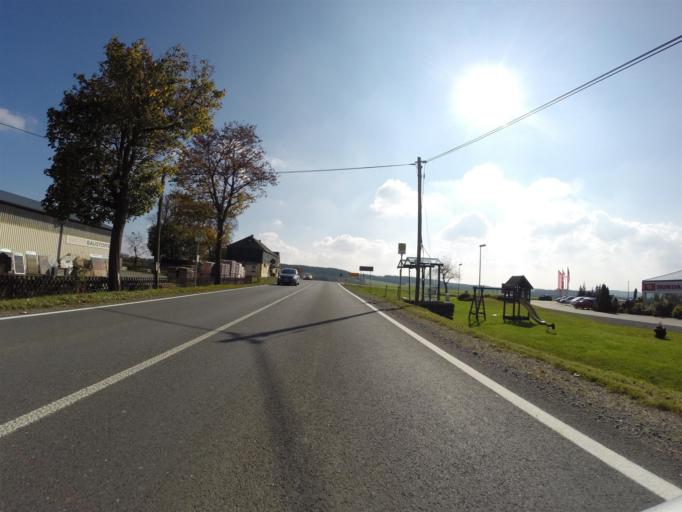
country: DE
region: Thuringia
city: Tanna
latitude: 50.4938
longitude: 11.8347
